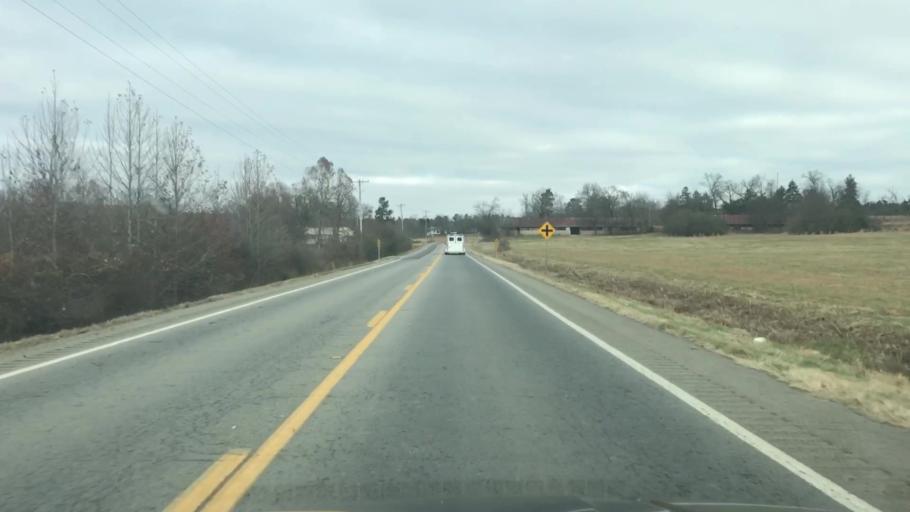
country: US
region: Arkansas
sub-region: Scott County
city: Waldron
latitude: 34.9450
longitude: -94.1037
